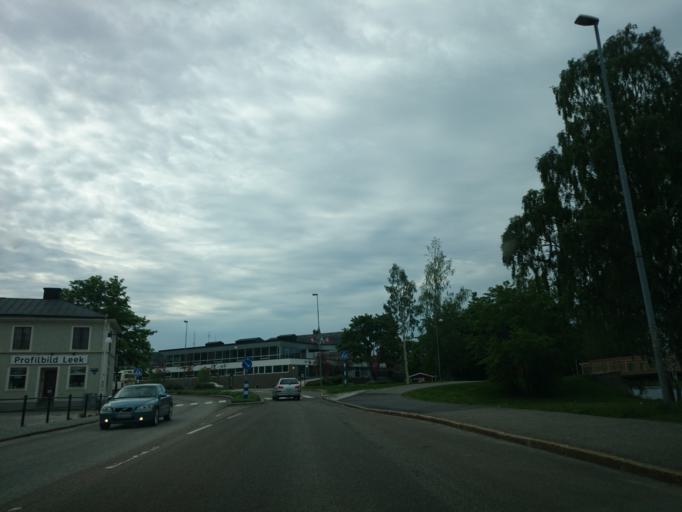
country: SE
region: Vaesternorrland
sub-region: Haernoesands Kommun
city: Haernoesand
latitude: 62.6295
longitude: 17.9394
